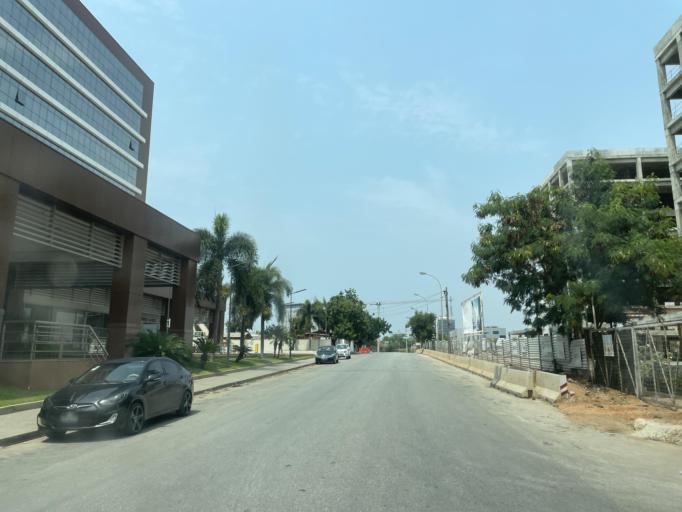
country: AO
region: Luanda
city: Luanda
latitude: -8.9234
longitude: 13.1908
